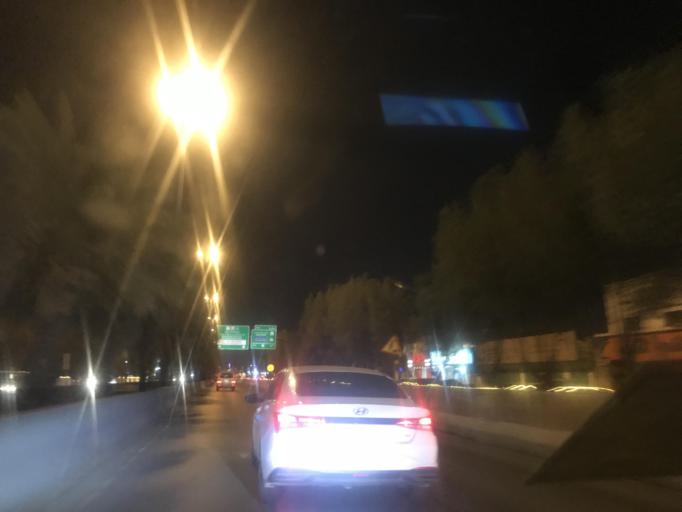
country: SA
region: Ar Riyad
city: Riyadh
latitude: 24.7570
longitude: 46.6852
